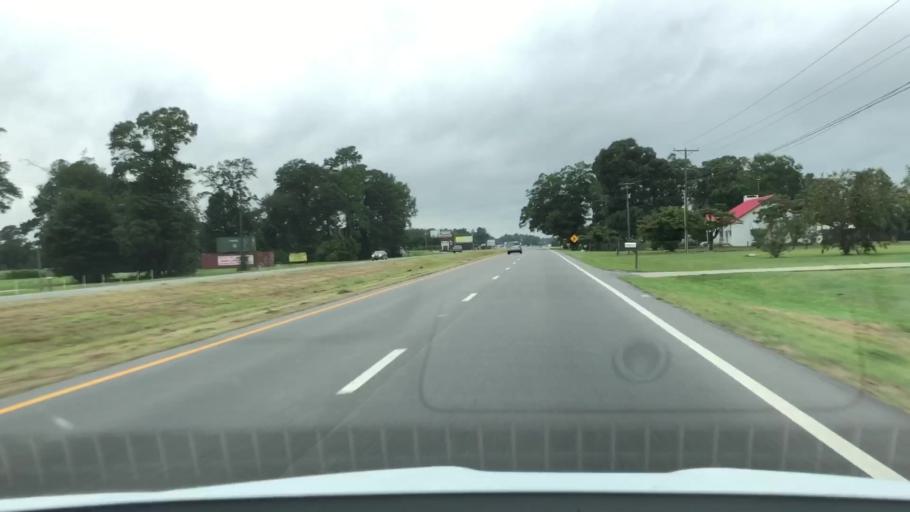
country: US
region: North Carolina
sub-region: Lenoir County
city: La Grange
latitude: 35.2794
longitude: -77.7496
